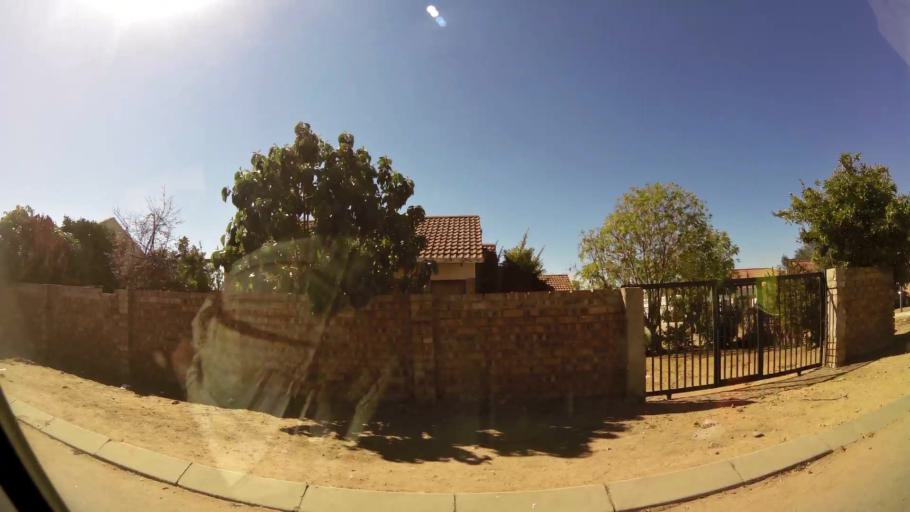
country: ZA
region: Limpopo
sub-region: Capricorn District Municipality
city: Polokwane
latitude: -23.8682
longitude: 29.4257
